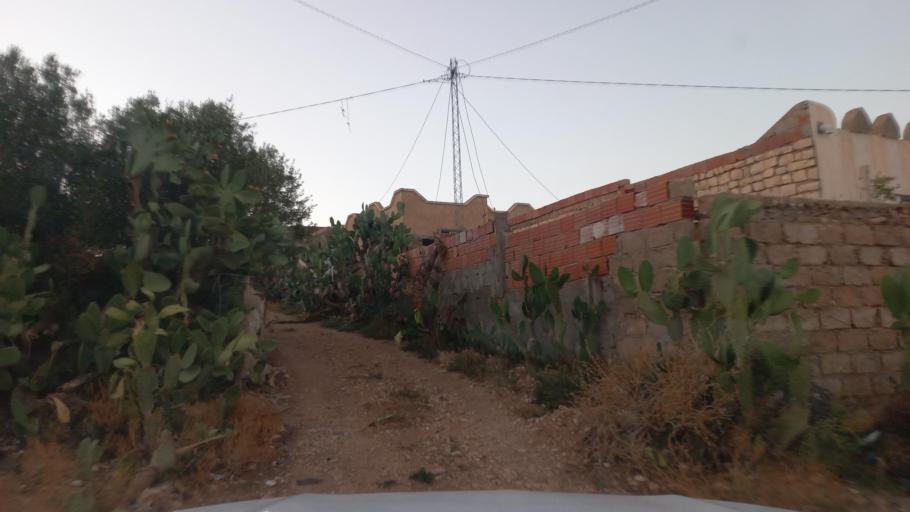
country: TN
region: Al Qasrayn
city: Sbiba
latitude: 35.3782
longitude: 9.0143
